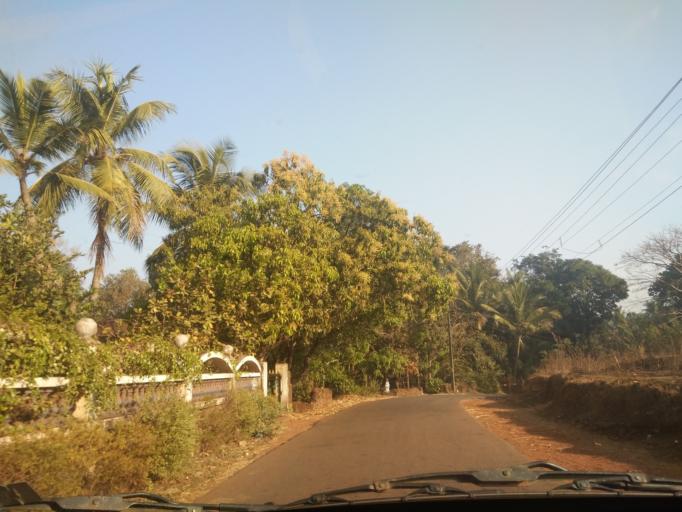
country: IN
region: Goa
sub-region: South Goa
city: Davorlim
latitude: 15.2862
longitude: 74.0065
